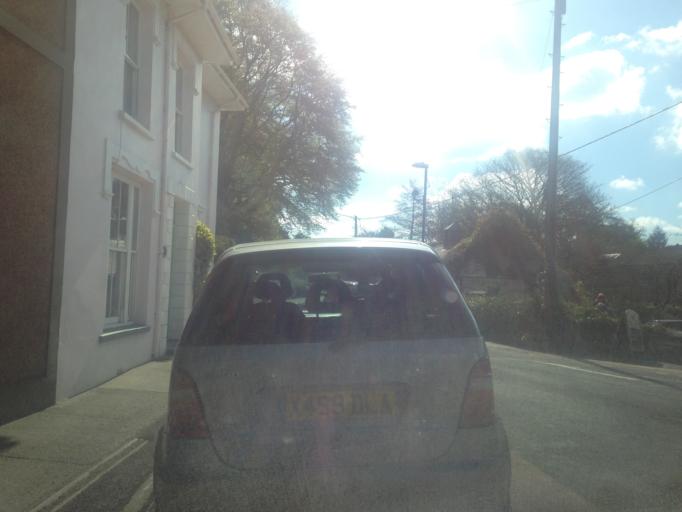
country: GB
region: Wales
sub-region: County of Ceredigion
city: Newcastle Emlyn
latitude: 52.0407
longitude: -4.4667
